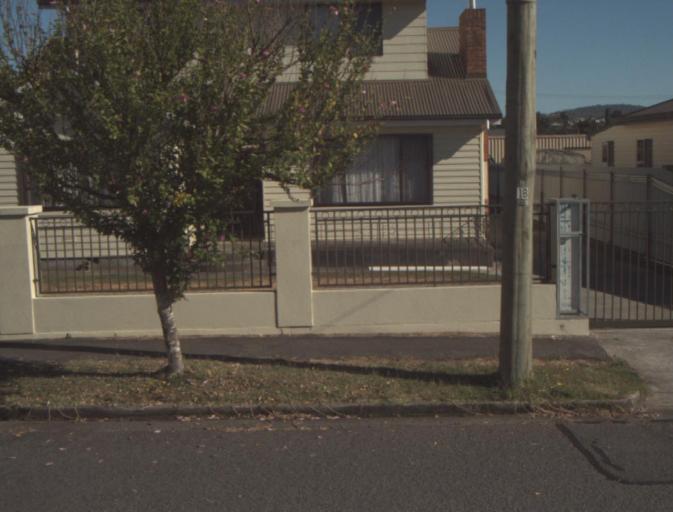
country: AU
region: Tasmania
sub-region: Launceston
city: Newnham
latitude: -41.4020
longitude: 147.1349
